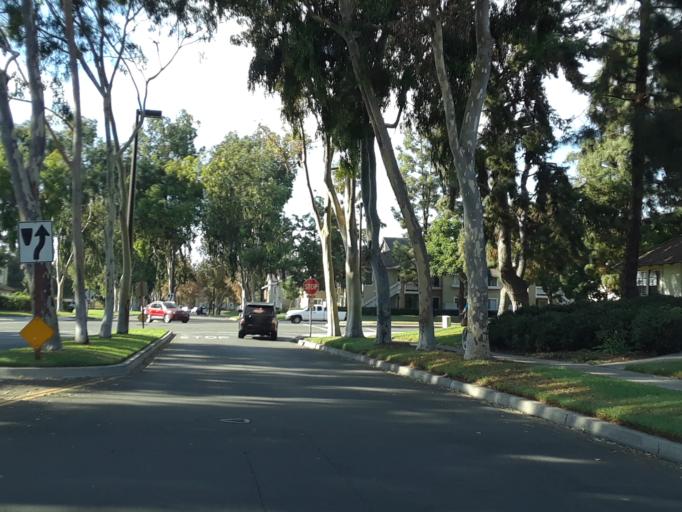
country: US
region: California
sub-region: Orange County
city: Irvine
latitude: 33.6768
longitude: -117.8107
